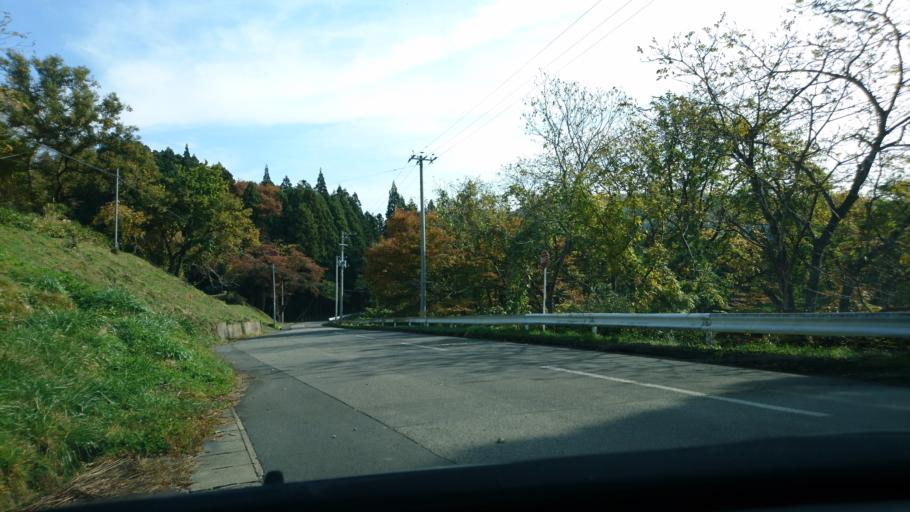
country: JP
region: Iwate
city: Ichinoseki
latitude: 38.9774
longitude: 141.1759
